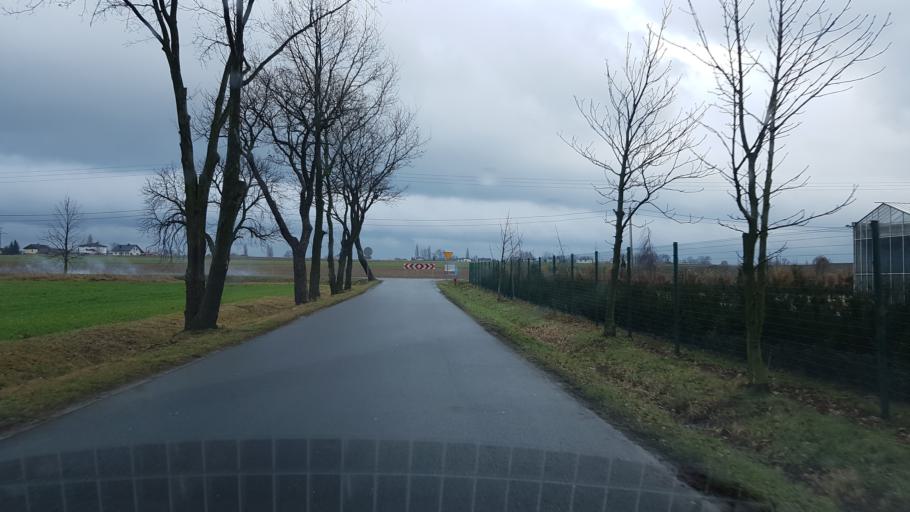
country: PL
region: Silesian Voivodeship
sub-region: Powiat pszczynski
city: Radostowice
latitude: 49.9675
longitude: 18.9075
